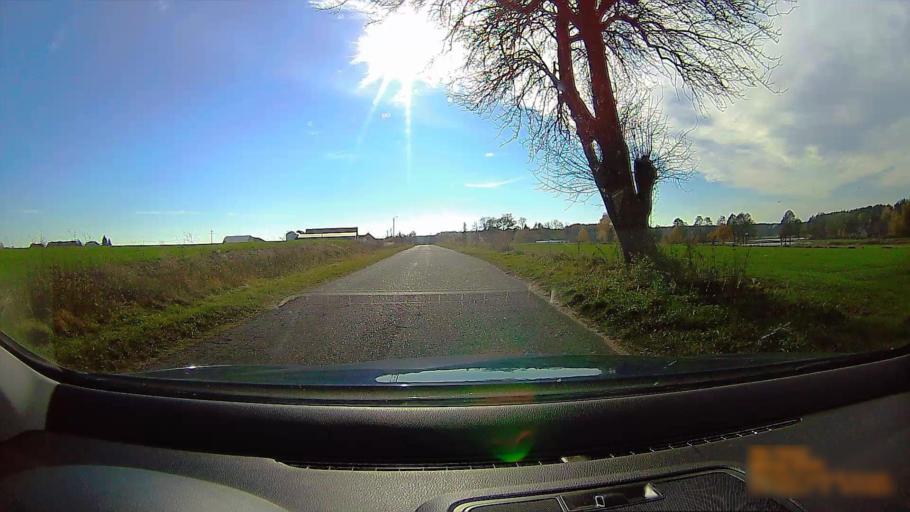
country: PL
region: Greater Poland Voivodeship
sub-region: Powiat ostrzeszowski
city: Doruchow
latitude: 51.3979
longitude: 18.0302
